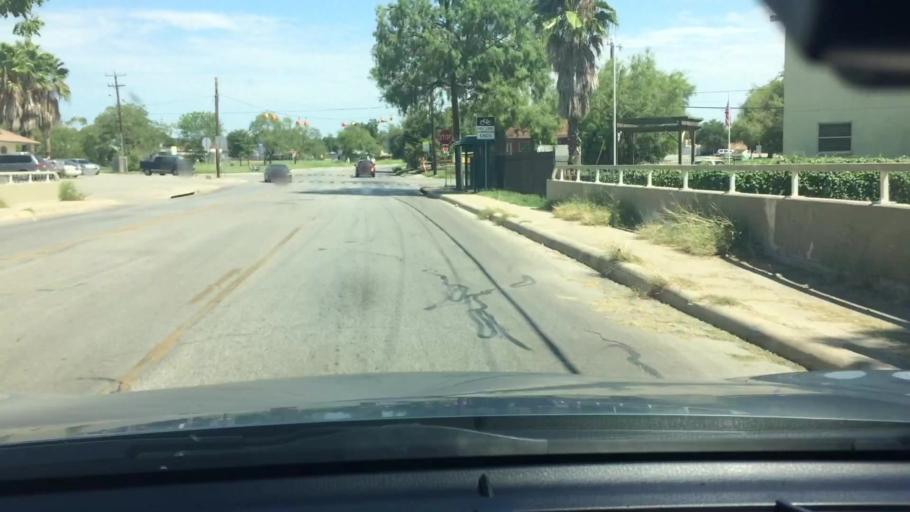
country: US
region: Texas
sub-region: Bexar County
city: San Antonio
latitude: 29.3954
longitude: -98.4332
